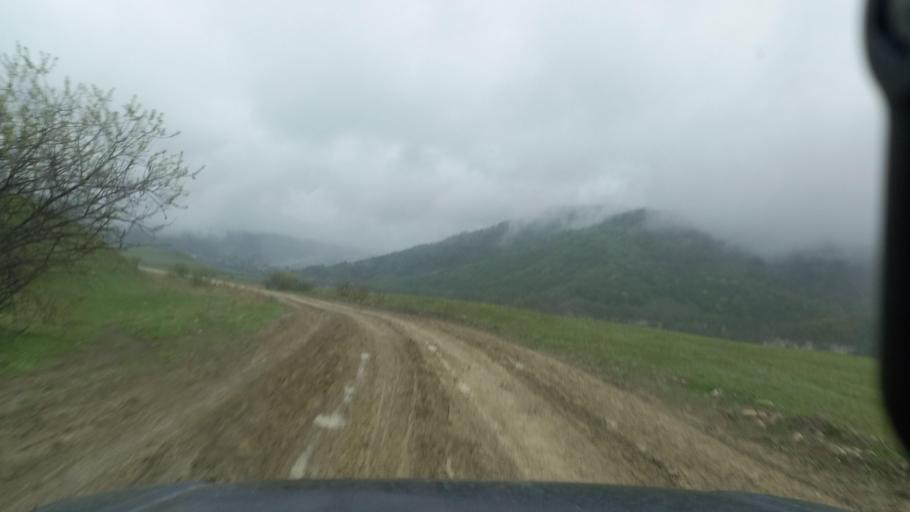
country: RU
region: Kabardino-Balkariya
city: Gundelen
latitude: 43.5938
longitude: 43.1265
